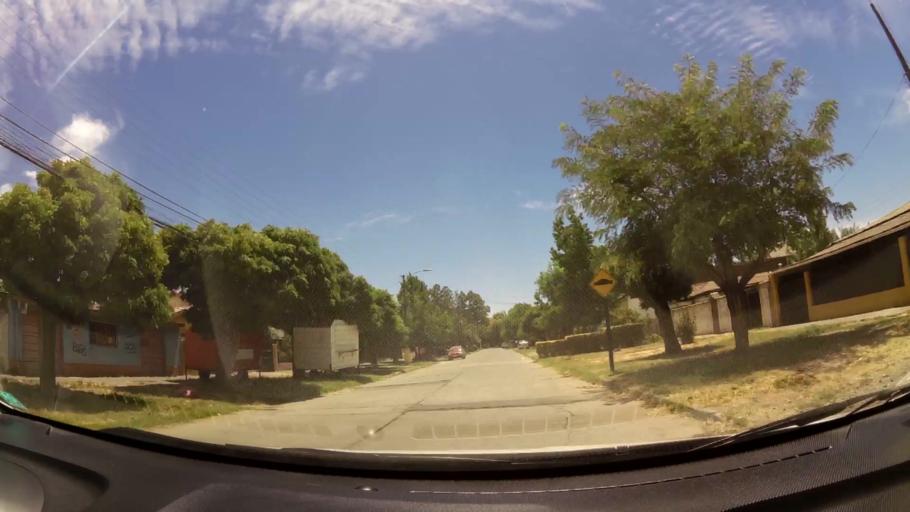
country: CL
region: O'Higgins
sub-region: Provincia de Cachapoal
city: Graneros
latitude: -34.0621
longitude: -70.7248
